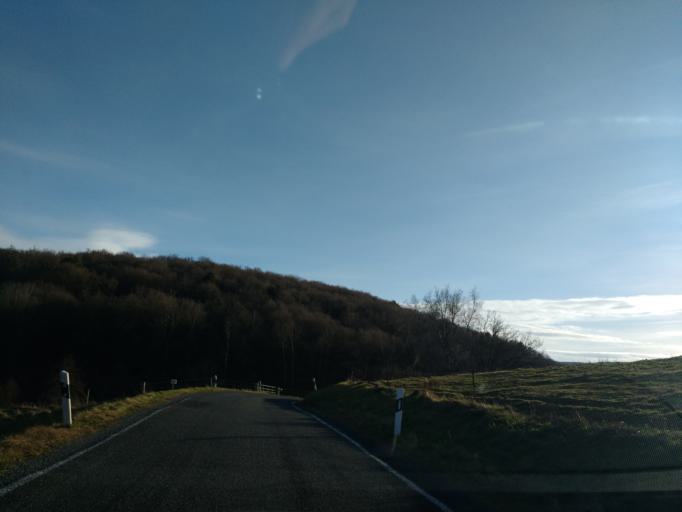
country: DE
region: Thuringia
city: Burgwalde
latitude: 51.3830
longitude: 10.0413
